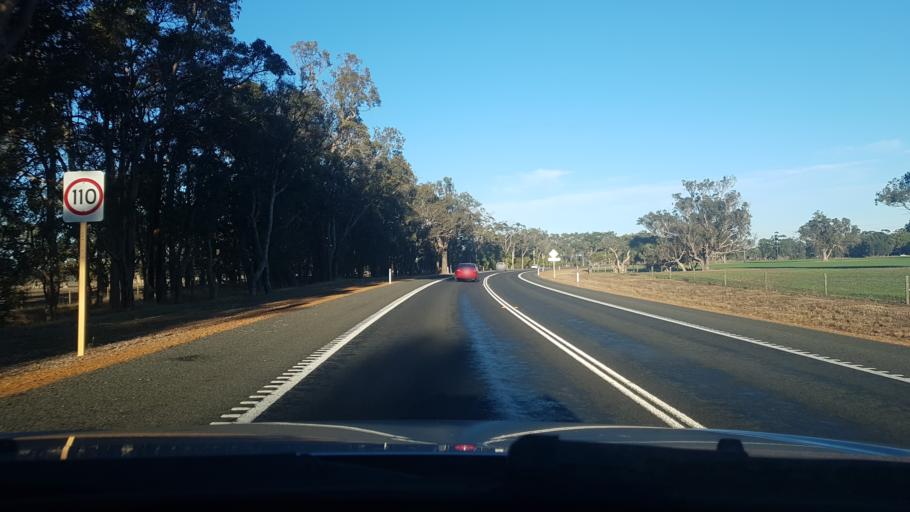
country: AU
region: Western Australia
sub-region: Busselton
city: Vasse
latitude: -33.6929
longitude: 115.2254
